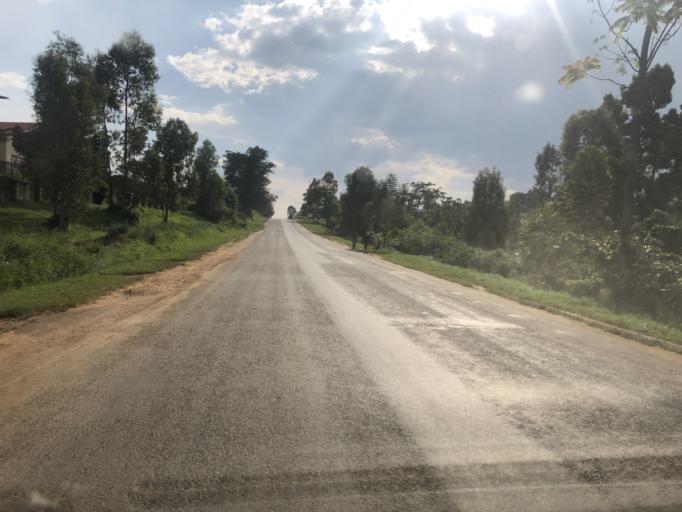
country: UG
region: Western Region
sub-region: Bushenyi District
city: Bushenyi
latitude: -0.5417
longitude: 30.1981
